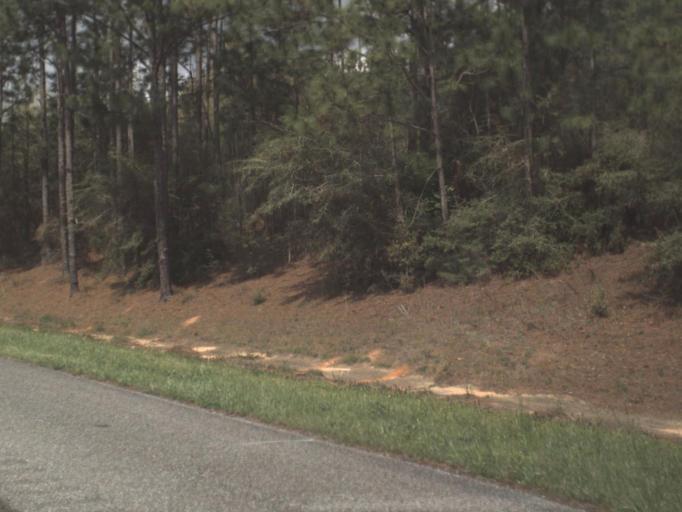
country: US
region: Florida
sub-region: Okaloosa County
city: Crestview
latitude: 30.6920
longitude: -86.7709
